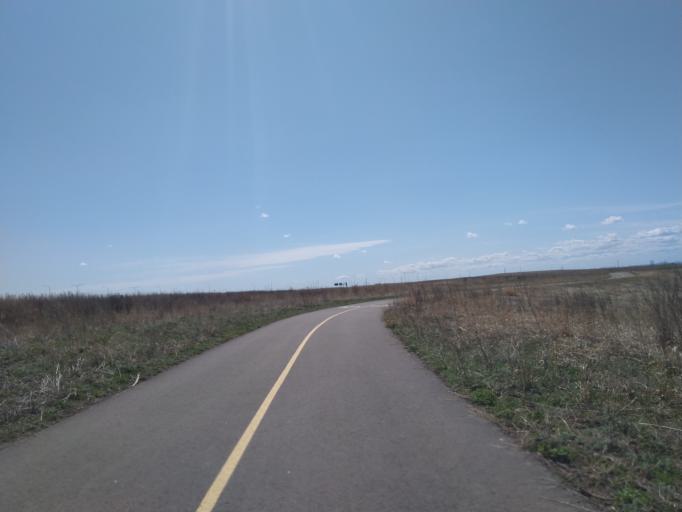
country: CA
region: Alberta
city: Chestermere
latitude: 51.0231
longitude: -113.9236
